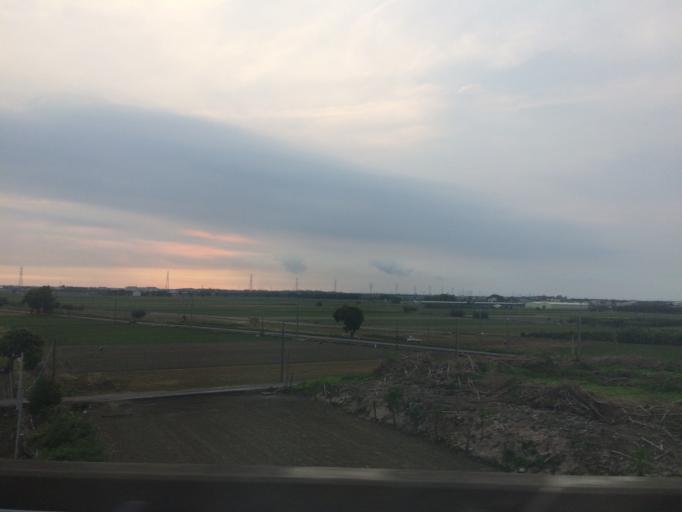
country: TW
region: Taiwan
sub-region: Yunlin
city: Douliu
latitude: 23.6659
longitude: 120.3702
